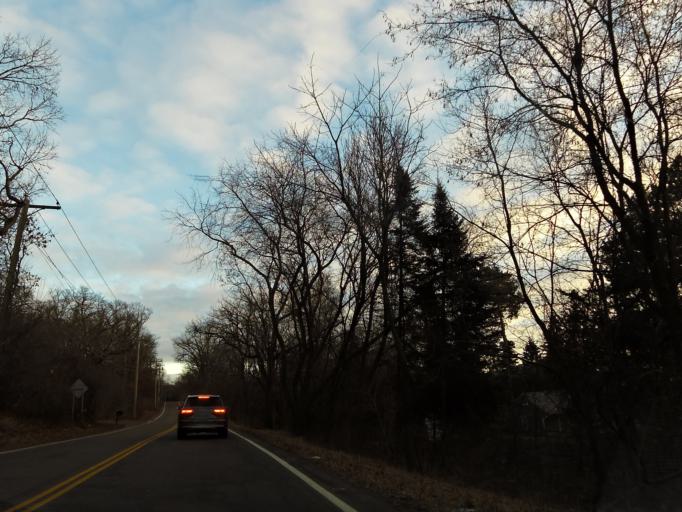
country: US
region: Minnesota
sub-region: Washington County
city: Dellwood
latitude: 45.0954
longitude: -92.9822
